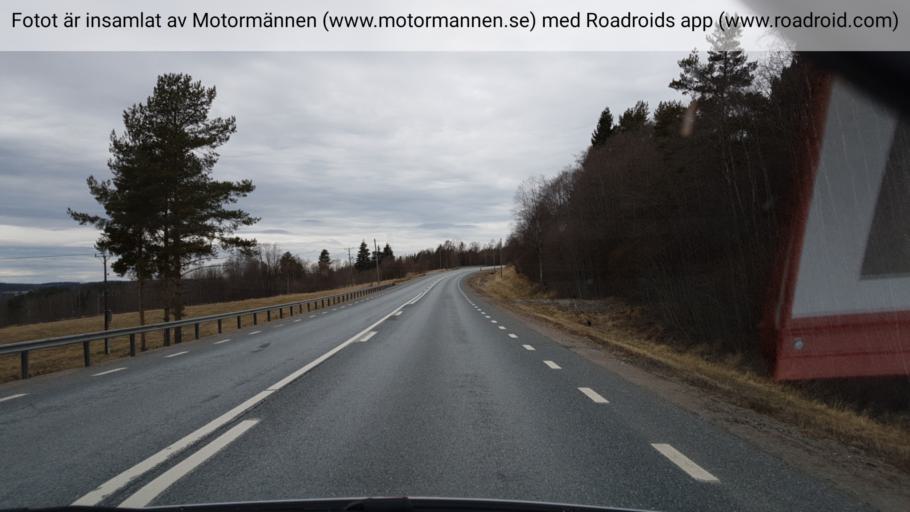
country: SE
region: Vaesternorrland
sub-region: Solleftea Kommun
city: Solleftea
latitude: 63.3513
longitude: 17.0501
